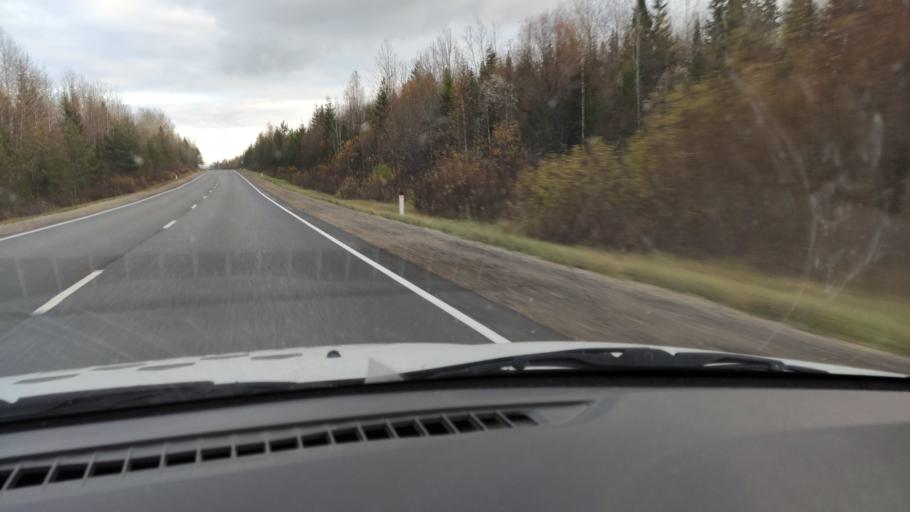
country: RU
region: Kirov
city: Omutninsk
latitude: 58.7059
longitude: 52.1046
